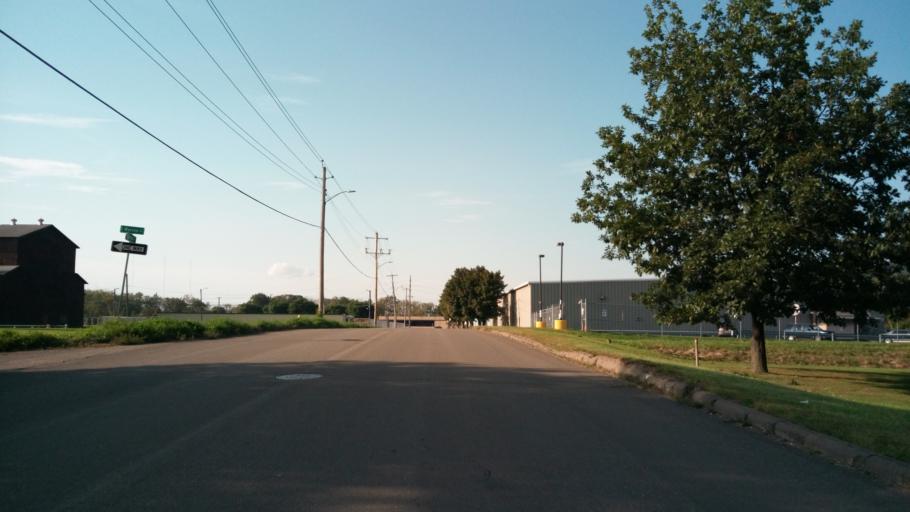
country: US
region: New York
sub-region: Chemung County
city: Elmira Heights
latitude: 42.1151
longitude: -76.8053
